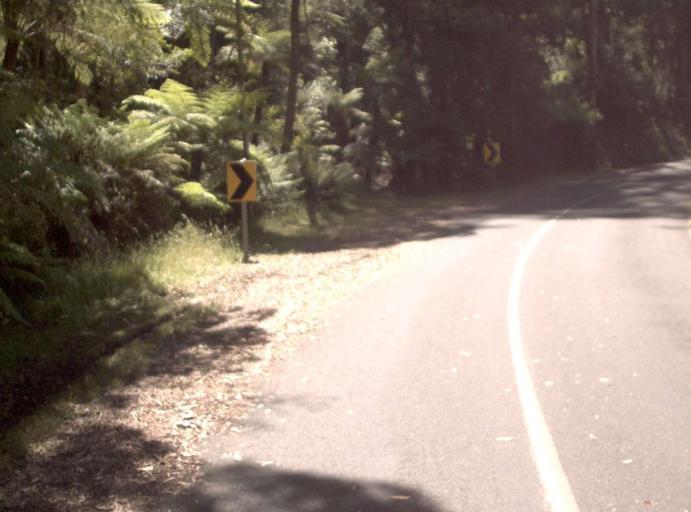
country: AU
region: Victoria
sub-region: Yarra Ranges
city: Millgrove
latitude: -37.7151
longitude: 145.7135
